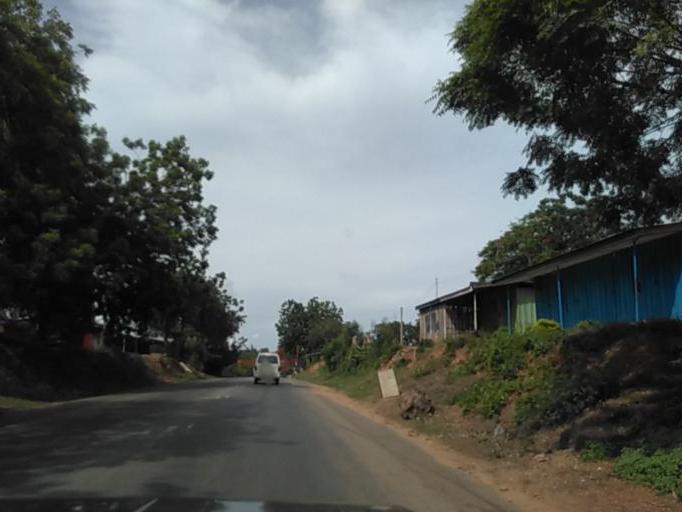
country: GH
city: Akropong
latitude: 6.2097
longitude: 0.0812
